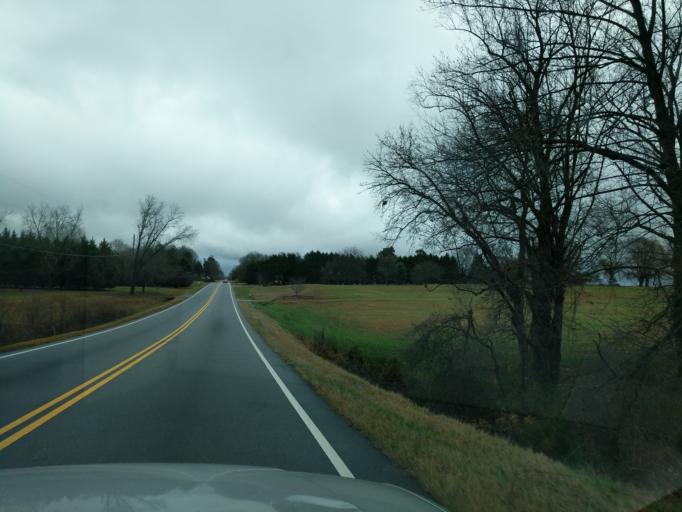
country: US
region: Georgia
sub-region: Hart County
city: Royston
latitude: 34.3556
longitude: -83.1045
